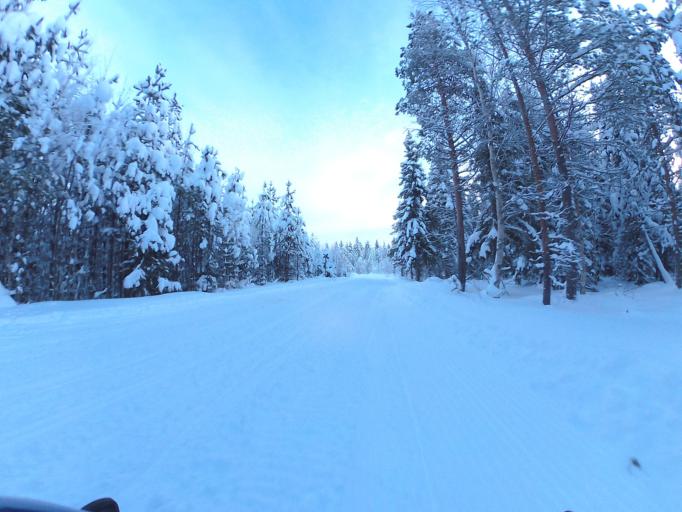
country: FI
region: Lapland
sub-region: Rovaniemi
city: Rovaniemi
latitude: 66.5188
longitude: 26.0099
